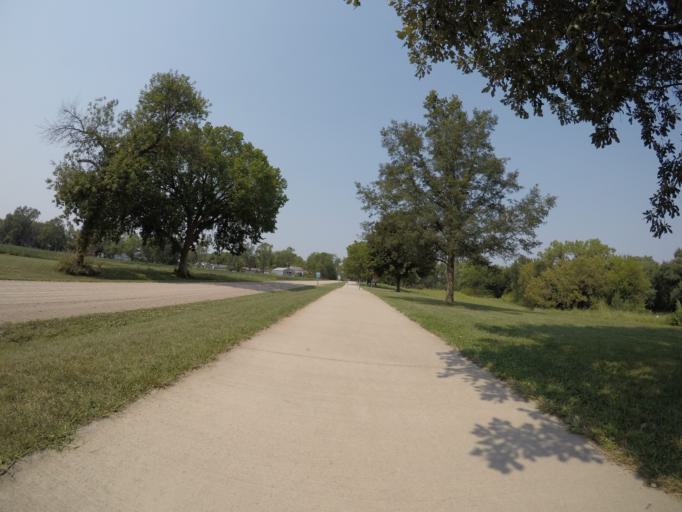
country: US
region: Nebraska
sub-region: Gage County
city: Beatrice
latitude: 40.2697
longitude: -96.7631
